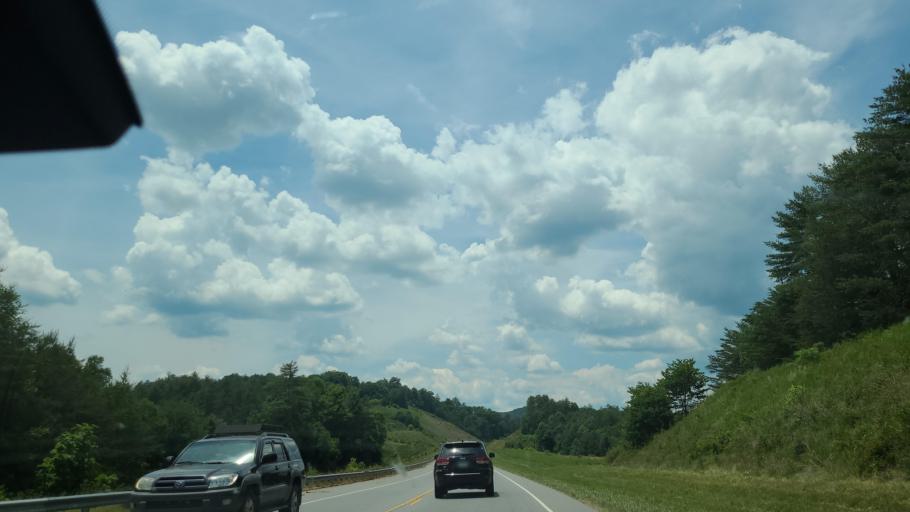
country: US
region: North Carolina
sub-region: Cherokee County
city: Murphy
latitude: 35.0708
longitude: -84.0051
